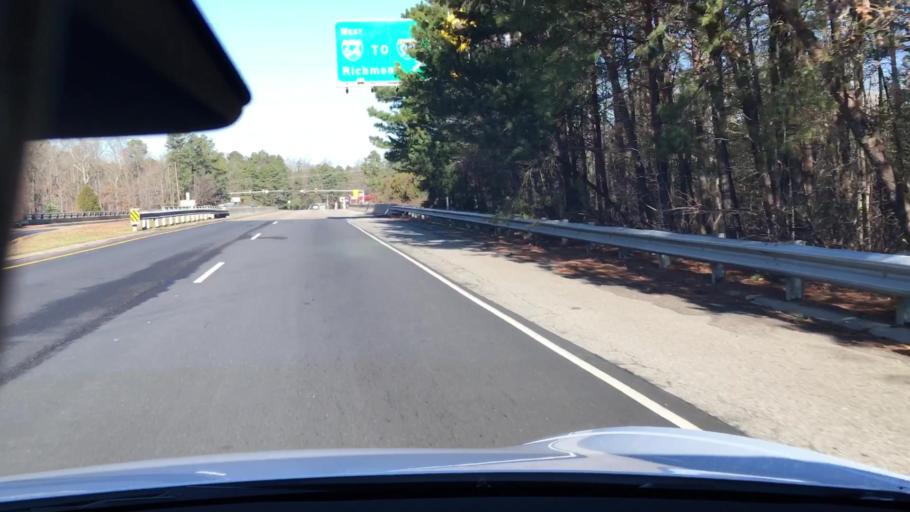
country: US
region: Virginia
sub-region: Henrico County
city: Montrose
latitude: 37.5312
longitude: -77.3603
